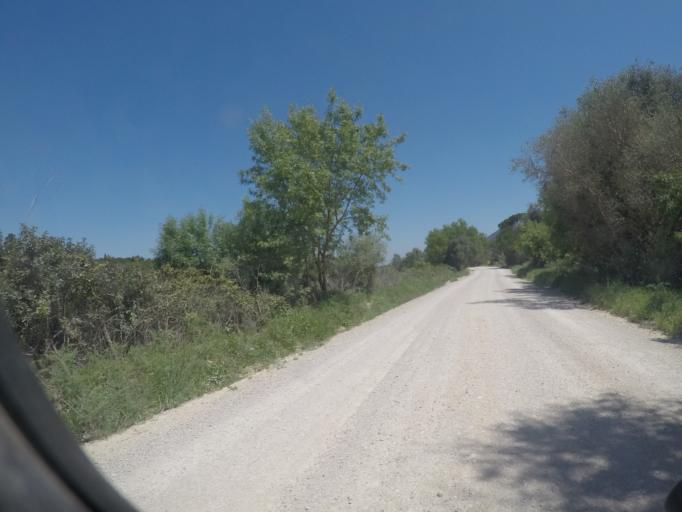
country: PT
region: Setubal
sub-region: Sesimbra
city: Sesimbra
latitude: 38.4627
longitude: -9.0538
